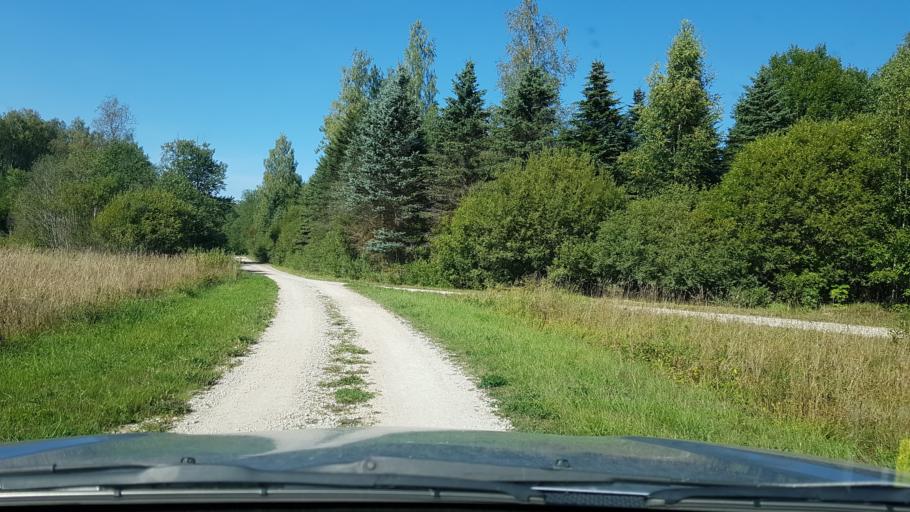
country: EE
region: Ida-Virumaa
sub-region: Sillamaee linn
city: Sillamae
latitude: 59.3311
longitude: 27.7736
